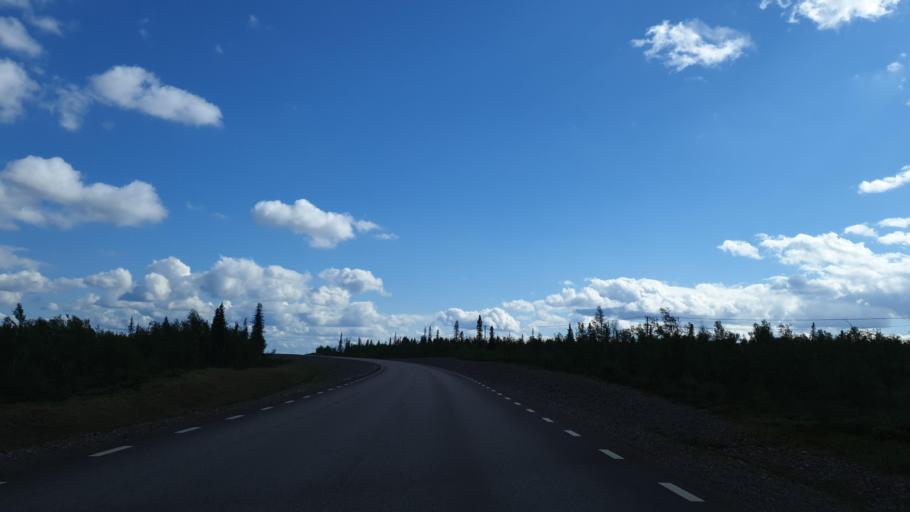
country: SE
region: Norrbotten
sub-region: Kiruna Kommun
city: Kiruna
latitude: 67.8066
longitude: 20.2334
